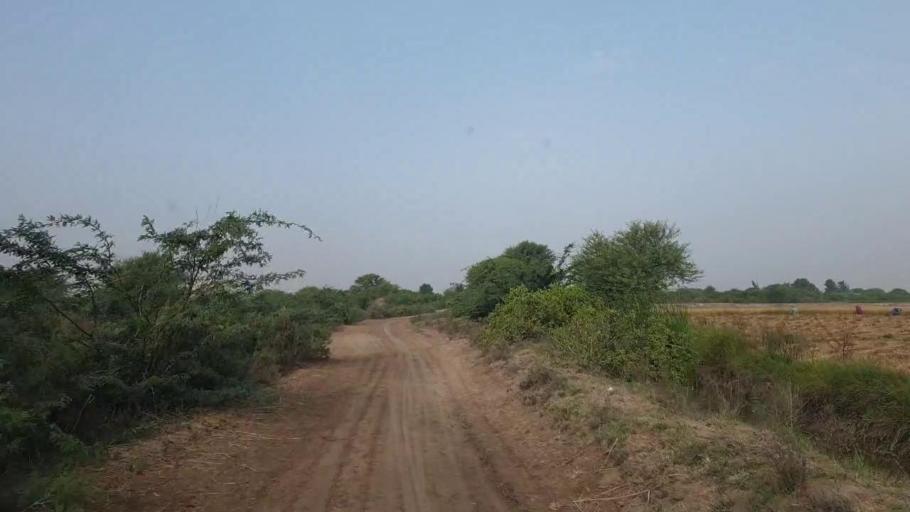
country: PK
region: Sindh
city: Talhar
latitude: 24.8412
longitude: 68.8010
